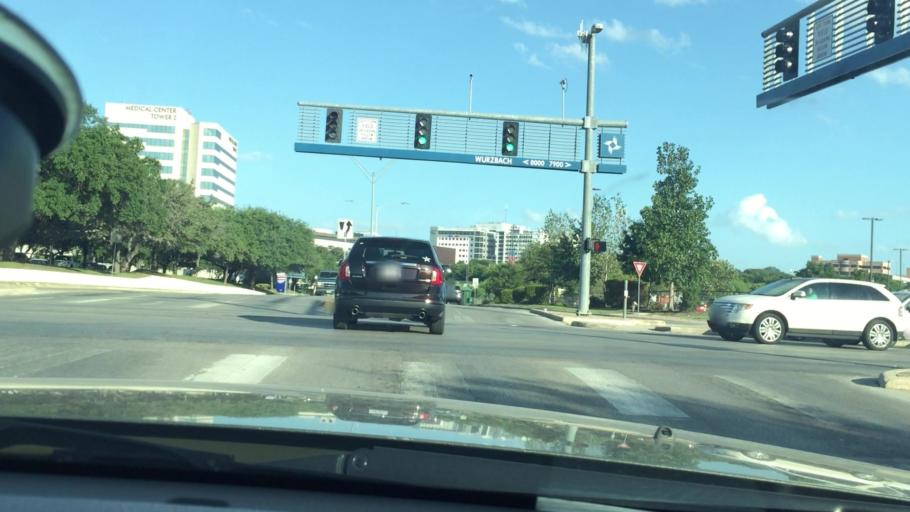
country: US
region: Texas
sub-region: Bexar County
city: Balcones Heights
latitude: 29.5136
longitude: -98.5783
